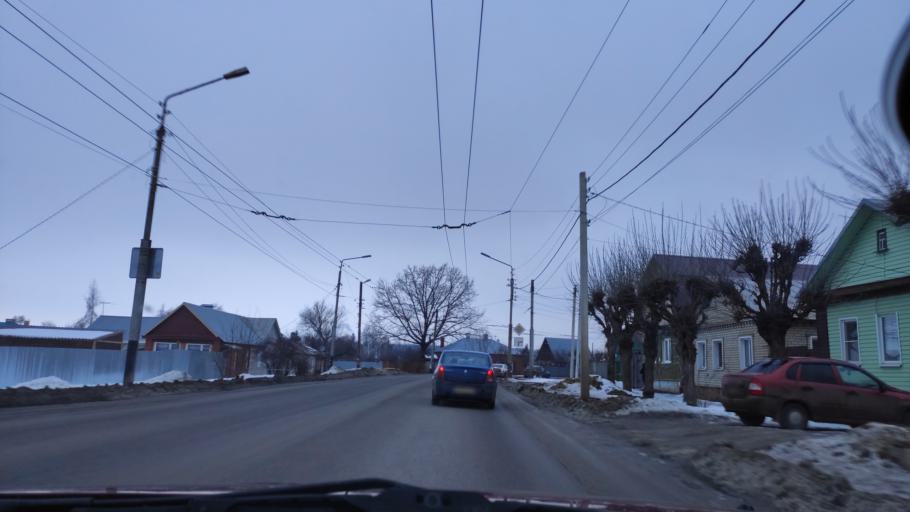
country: RU
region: Tambov
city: Tambov
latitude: 52.7041
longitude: 41.4561
